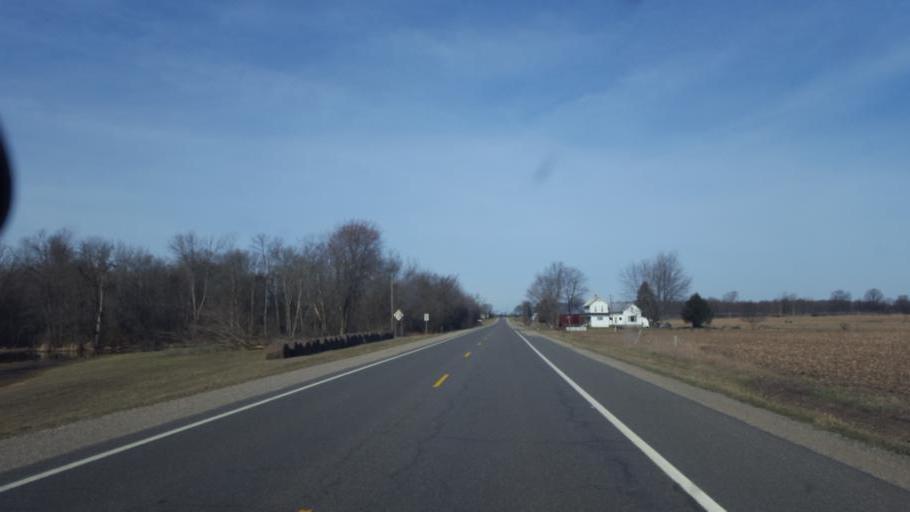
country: US
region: Michigan
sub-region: Montcalm County
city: Lakeview
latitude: 43.4325
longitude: -85.3509
